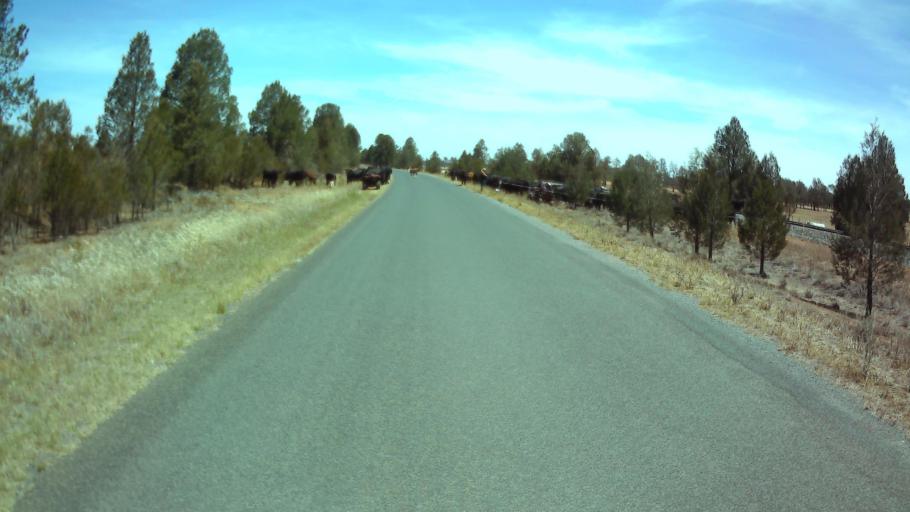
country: AU
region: New South Wales
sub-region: Weddin
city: Grenfell
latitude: -33.7781
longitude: 147.7540
